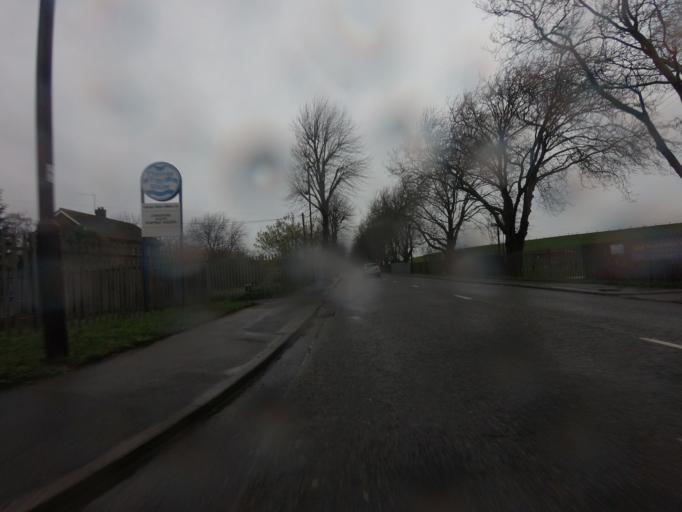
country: GB
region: England
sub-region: Greater London
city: Walthamstow
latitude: 51.6372
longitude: -0.0164
